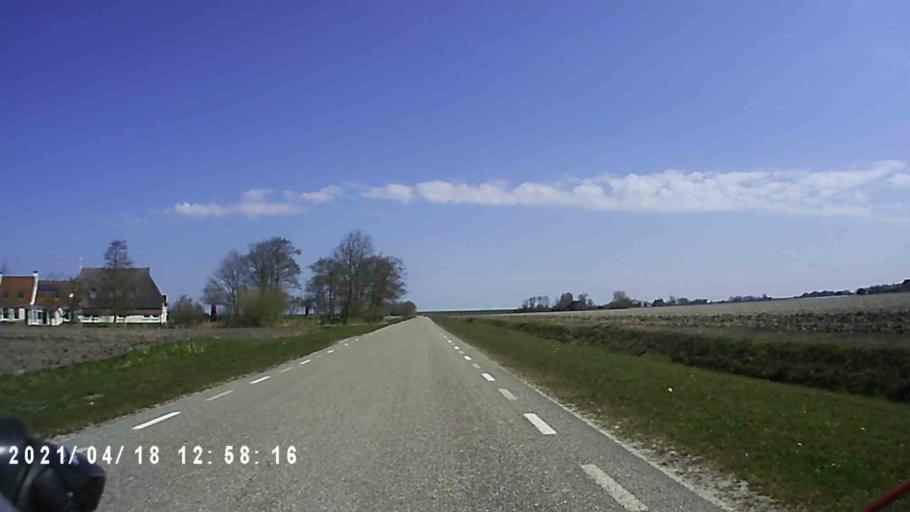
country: NL
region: Friesland
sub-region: Gemeente Dongeradeel
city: Anjum
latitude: 53.3952
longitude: 6.0884
